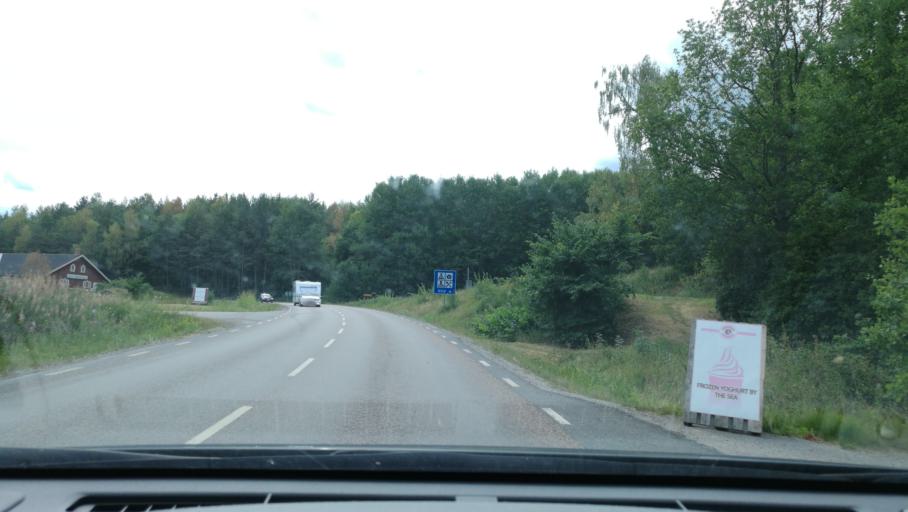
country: SE
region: OEstergoetland
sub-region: Norrkopings Kommun
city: Krokek
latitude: 58.6639
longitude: 16.4056
